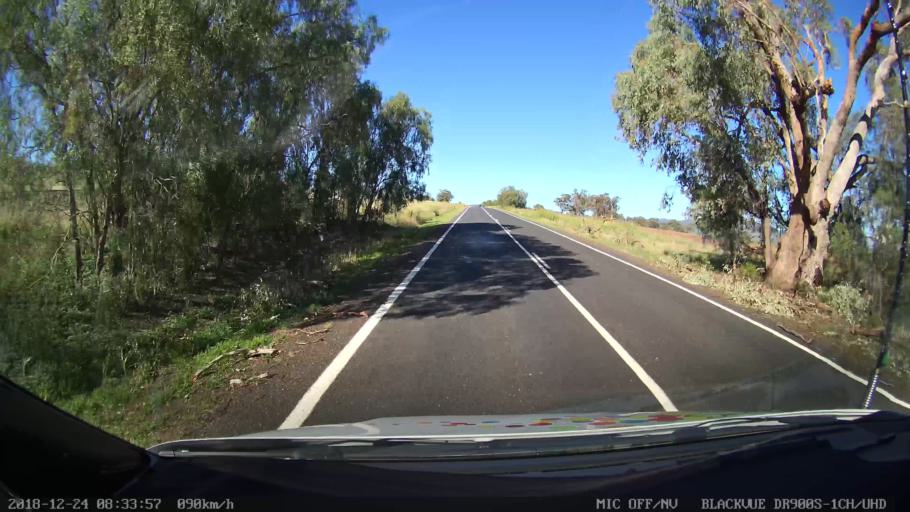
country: AU
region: New South Wales
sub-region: Liverpool Plains
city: Quirindi
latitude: -31.2896
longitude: 150.6773
